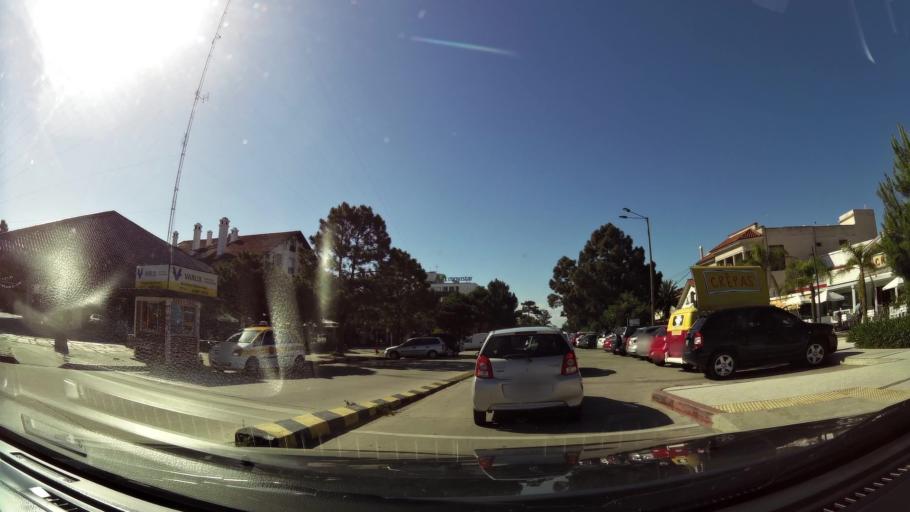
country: UY
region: Canelones
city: Barra de Carrasco
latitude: -34.8903
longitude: -56.0565
